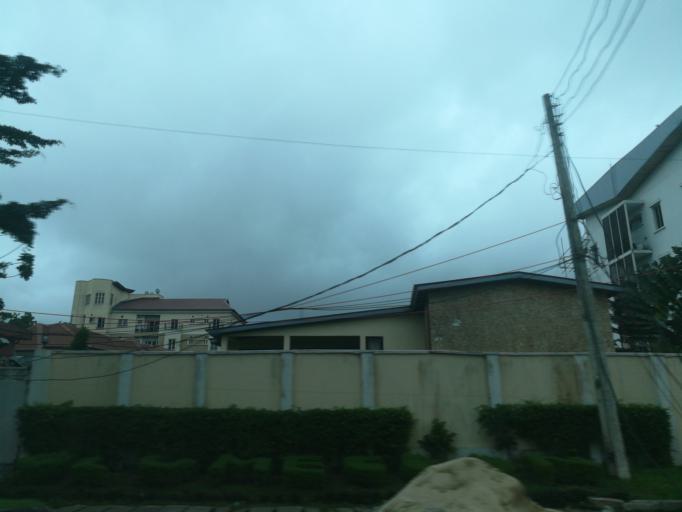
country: NG
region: Lagos
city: Ikoyi
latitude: 6.4254
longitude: 3.4240
